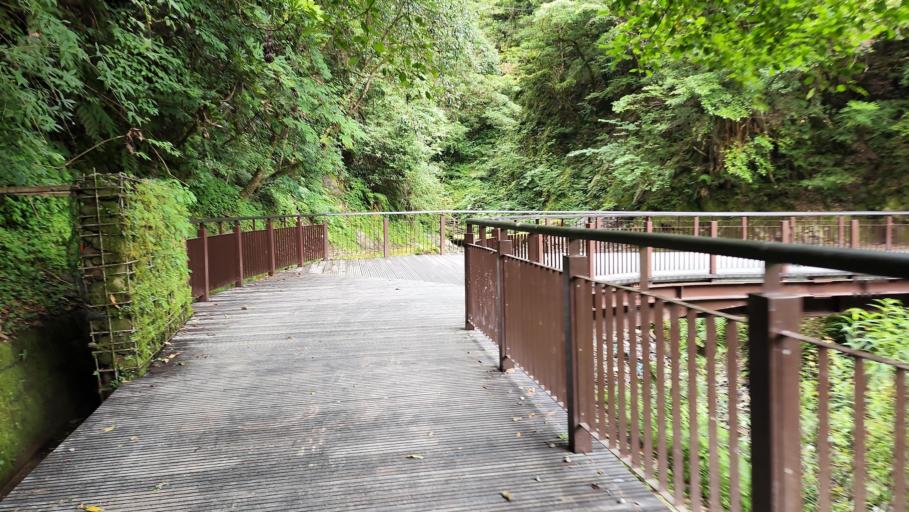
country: TW
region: Taiwan
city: Daxi
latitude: 24.7087
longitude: 121.4367
